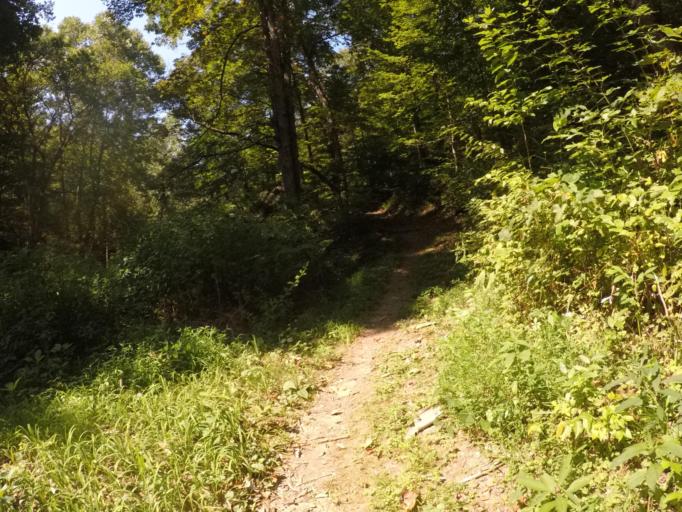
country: US
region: Ohio
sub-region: Lawrence County
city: Ironton
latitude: 38.6278
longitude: -82.6115
